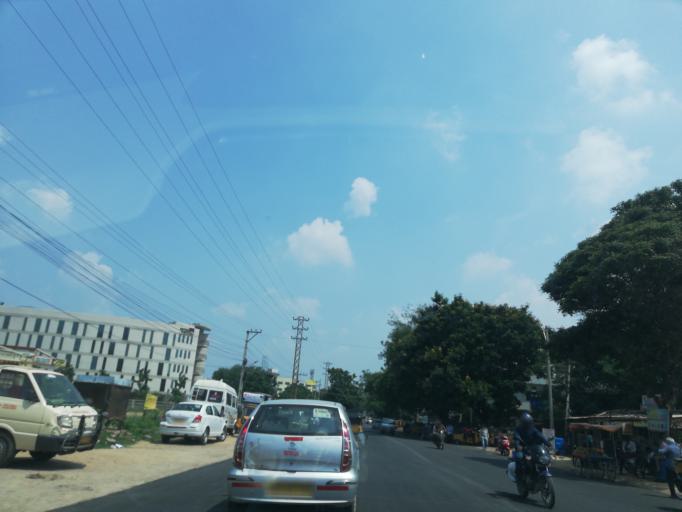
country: IN
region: Telangana
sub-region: Medak
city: Serilingampalle
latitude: 17.4807
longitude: 78.3201
